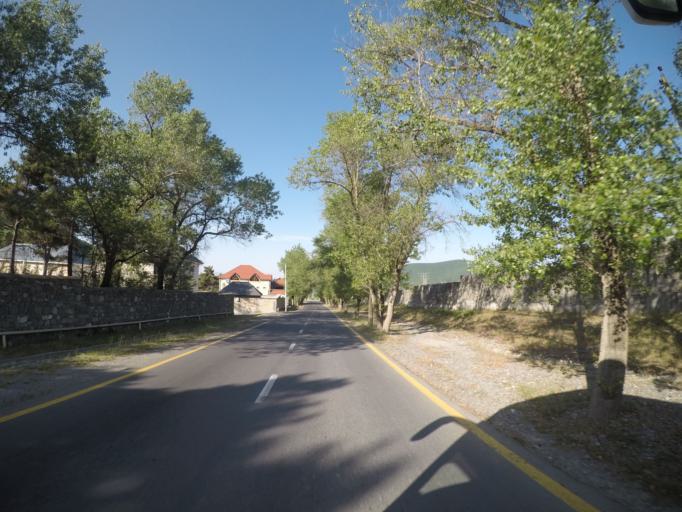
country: AZ
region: Shaki City
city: Sheki
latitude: 41.2382
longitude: 47.1833
